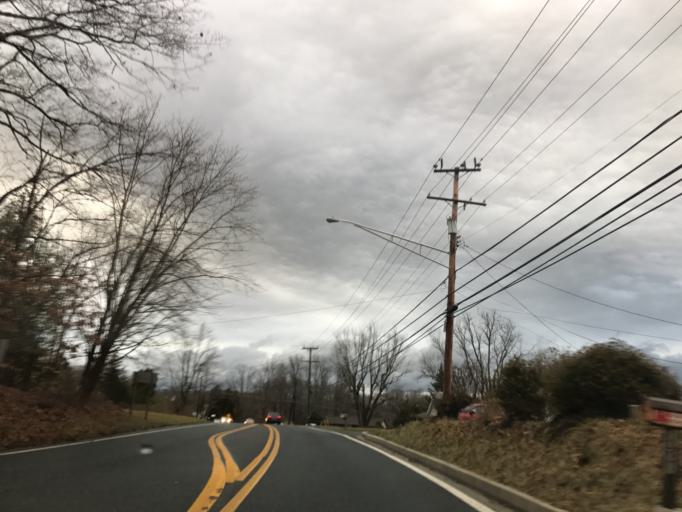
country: US
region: Maryland
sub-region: Harford County
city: South Bel Air
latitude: 39.5681
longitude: -76.3324
